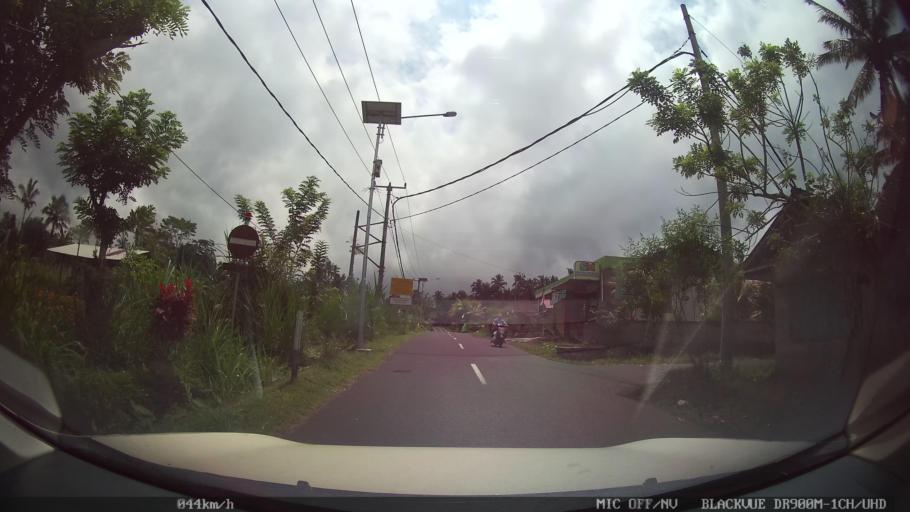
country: ID
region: Bali
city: Banjar Geriana Kangin
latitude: -8.4194
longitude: 115.4365
